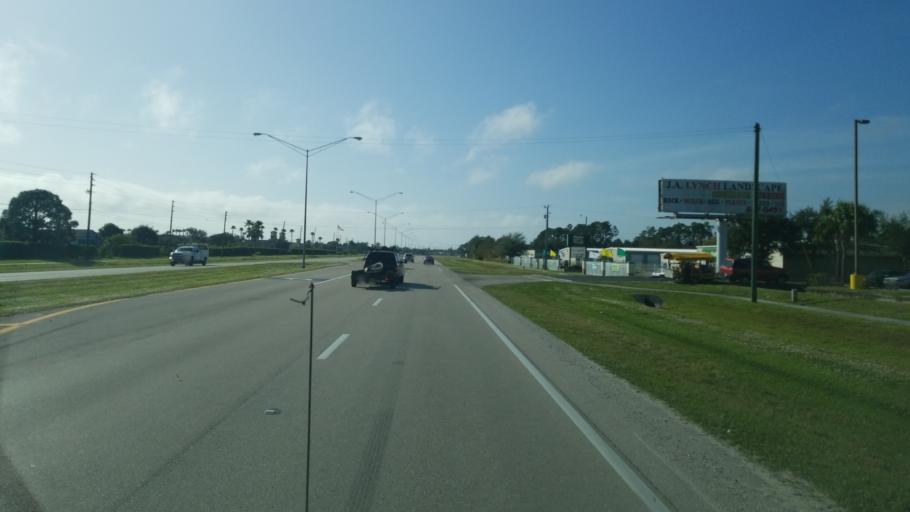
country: US
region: Florida
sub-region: Charlotte County
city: Port Charlotte
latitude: 27.0116
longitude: -82.0536
